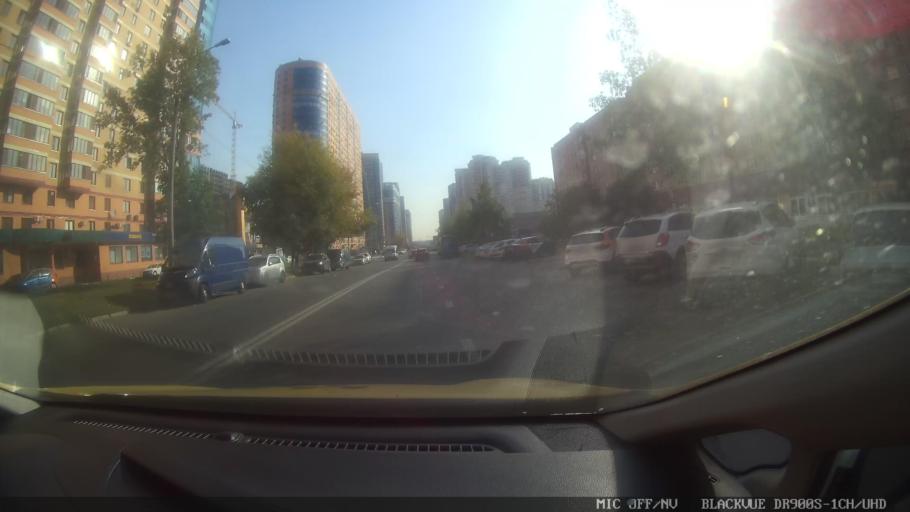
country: RU
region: Moskovskaya
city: Reutov
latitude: 55.7518
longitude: 37.8716
